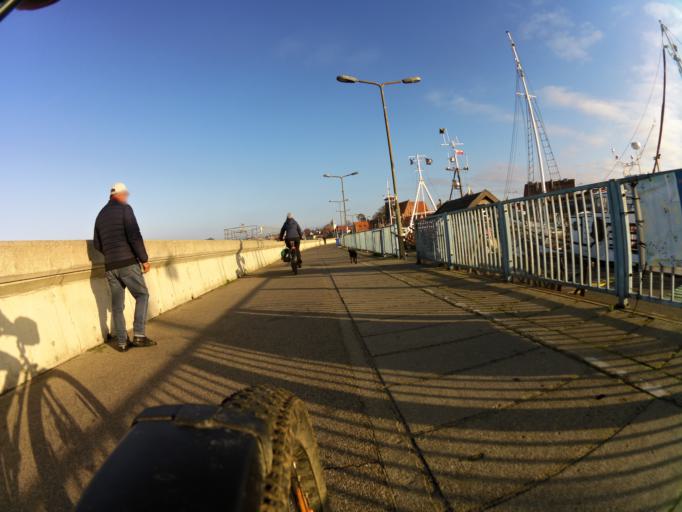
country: PL
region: Pomeranian Voivodeship
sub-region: Powiat pucki
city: Hel
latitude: 54.6038
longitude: 18.8005
